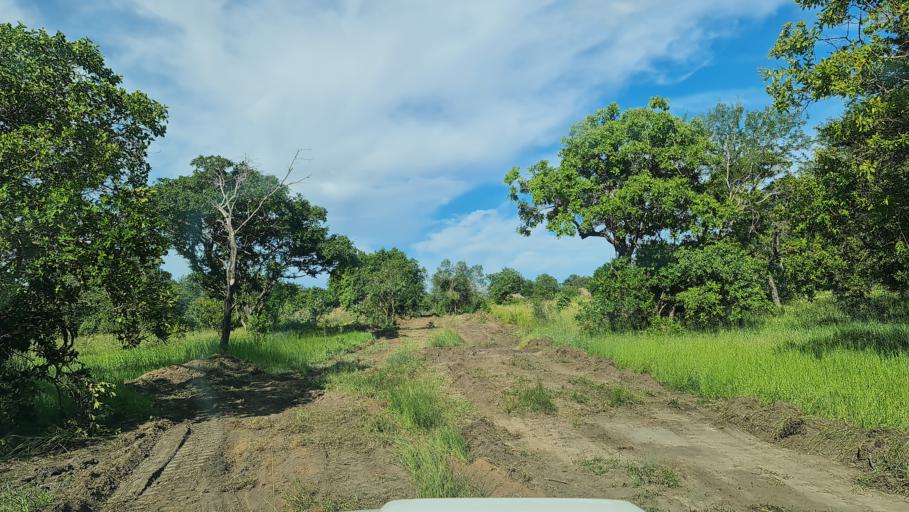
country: MZ
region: Nampula
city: Ilha de Mocambique
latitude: -15.5061
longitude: 40.1485
